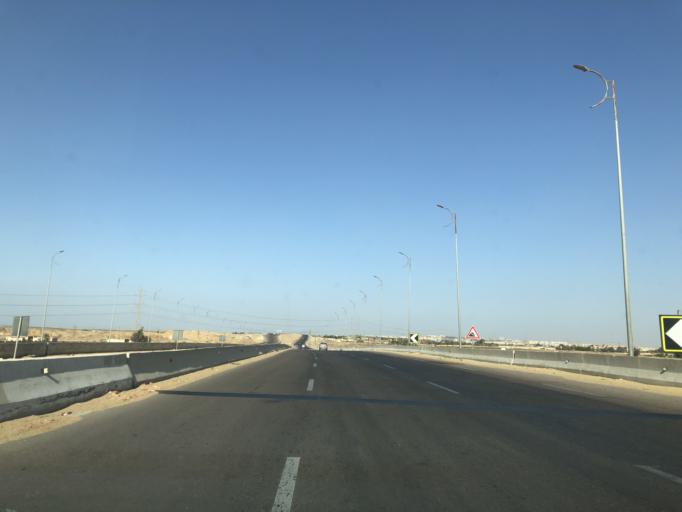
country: EG
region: Al Jizah
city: Awsim
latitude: 30.0691
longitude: 30.9067
